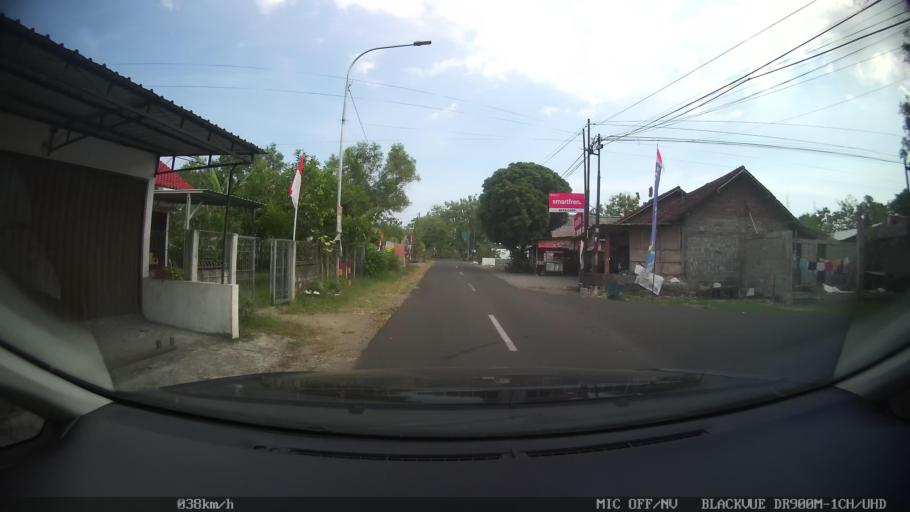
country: ID
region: Daerah Istimewa Yogyakarta
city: Bantul
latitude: -7.8616
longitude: 110.3077
